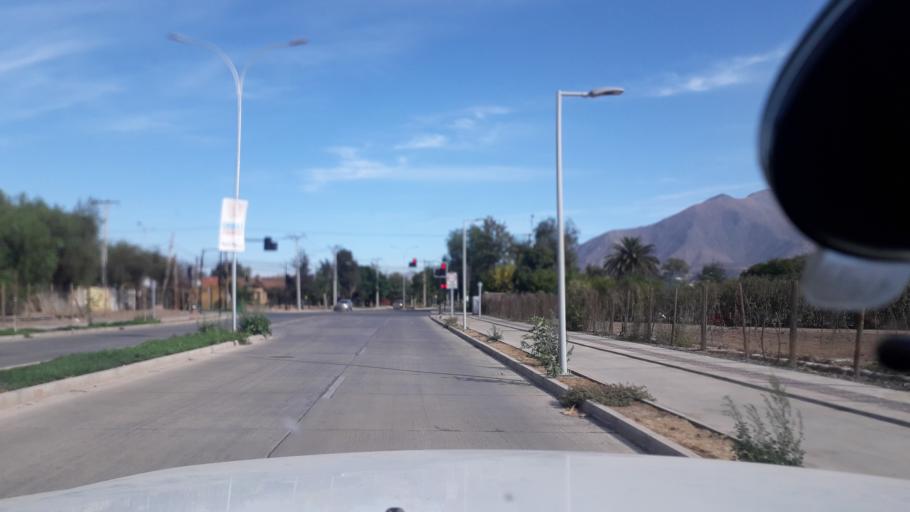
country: CL
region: Valparaiso
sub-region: Provincia de San Felipe
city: San Felipe
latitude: -32.7492
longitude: -70.7109
